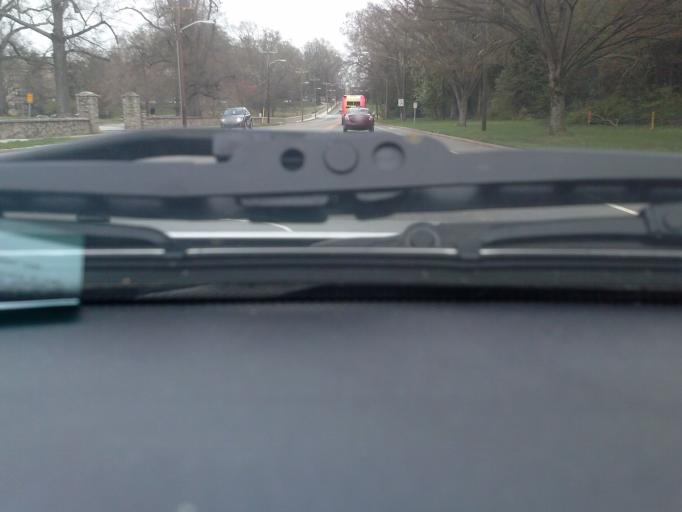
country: US
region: North Carolina
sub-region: Durham County
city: Durham
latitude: 36.0053
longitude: -78.9184
